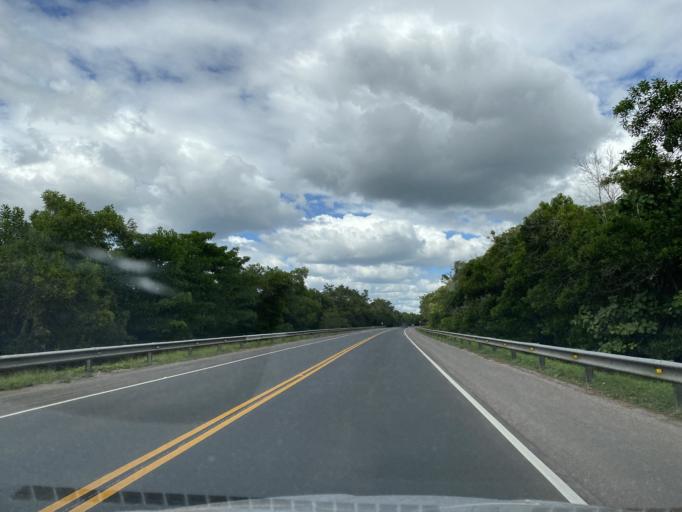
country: DO
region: Santo Domingo
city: Guerra
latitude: 18.6008
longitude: -69.7710
